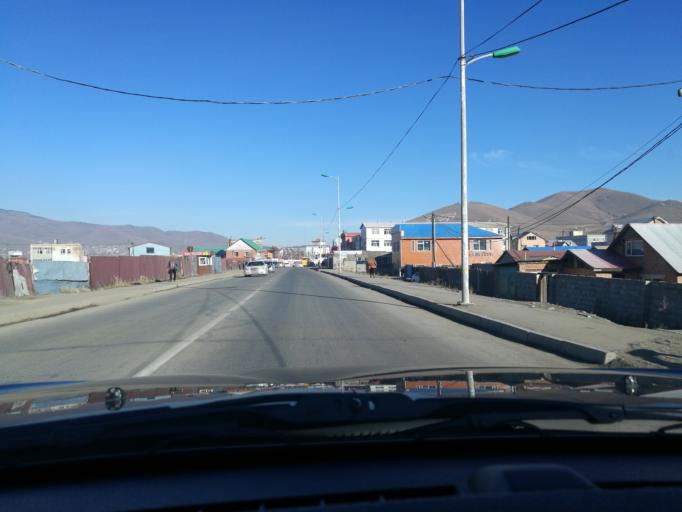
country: MN
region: Ulaanbaatar
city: Ulaanbaatar
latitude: 47.9789
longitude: 106.9388
